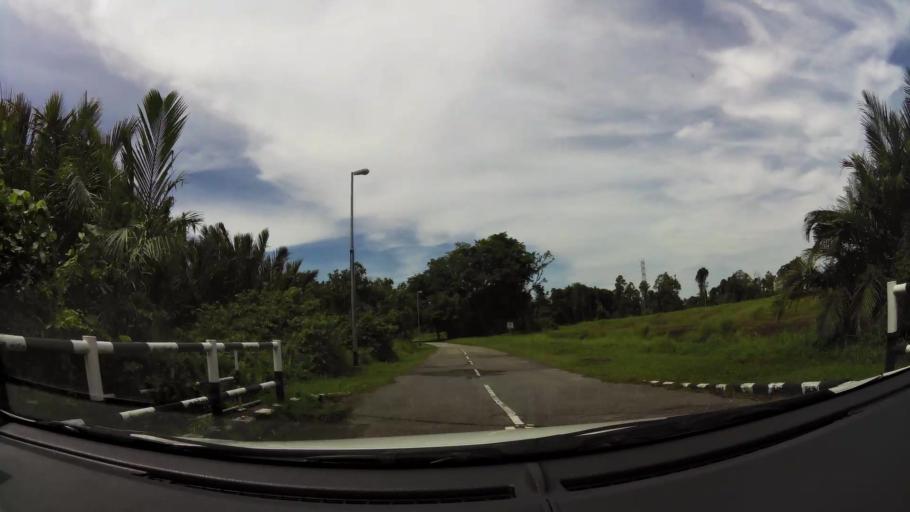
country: BN
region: Belait
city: Seria
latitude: 4.5959
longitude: 114.2837
